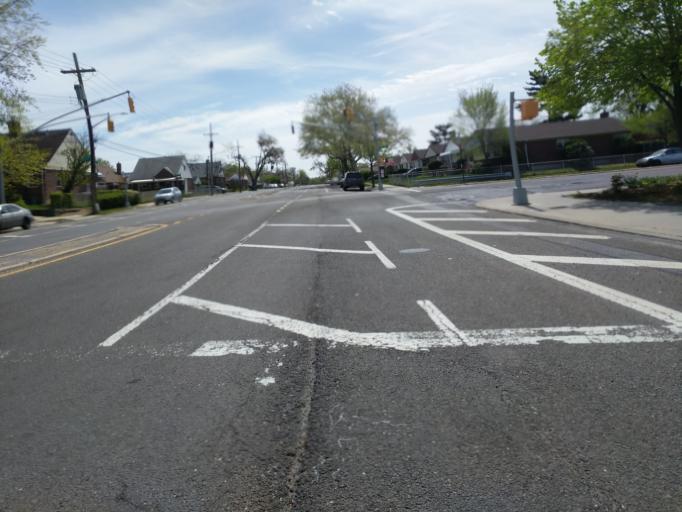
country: US
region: New York
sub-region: Nassau County
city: Elmont
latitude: 40.6856
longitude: -73.7340
